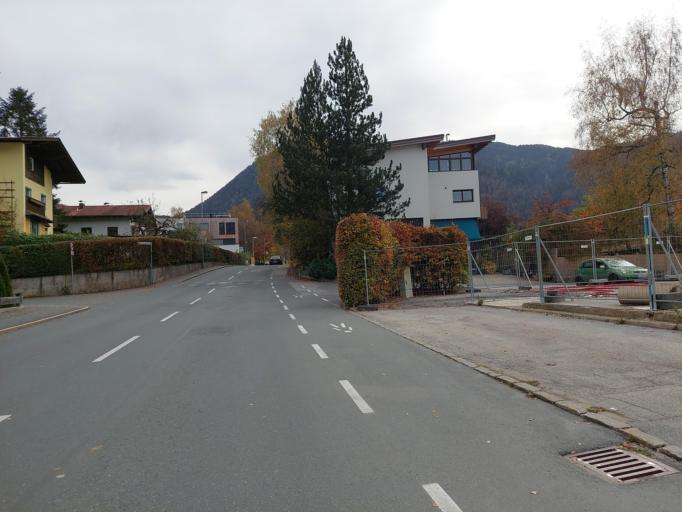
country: AT
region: Tyrol
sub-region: Politischer Bezirk Kufstein
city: Worgl
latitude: 47.4863
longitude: 12.0580
